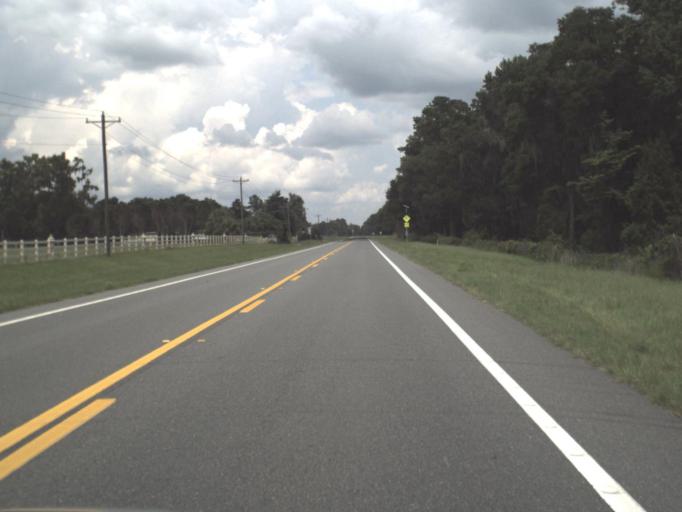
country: US
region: Florida
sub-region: Alachua County
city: Alachua
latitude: 29.8120
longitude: -82.4676
